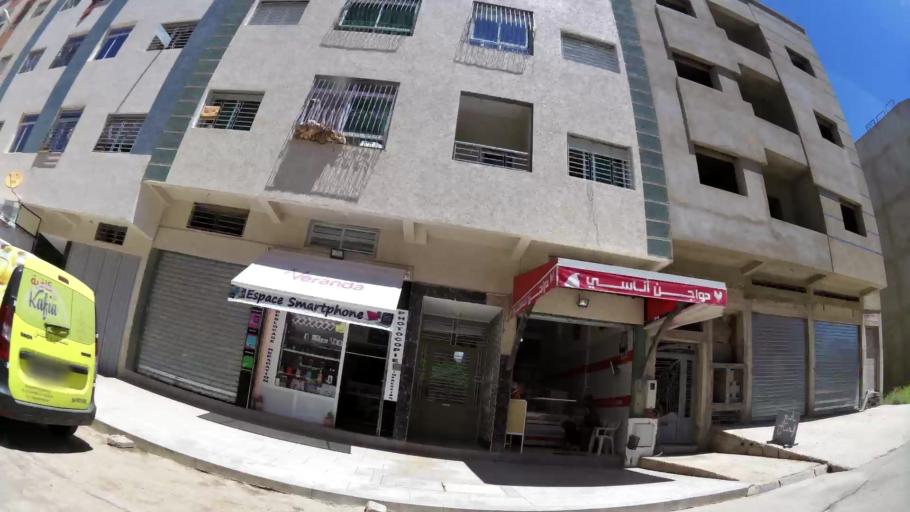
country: MA
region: Meknes-Tafilalet
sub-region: Meknes
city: Meknes
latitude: 33.8545
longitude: -5.5636
